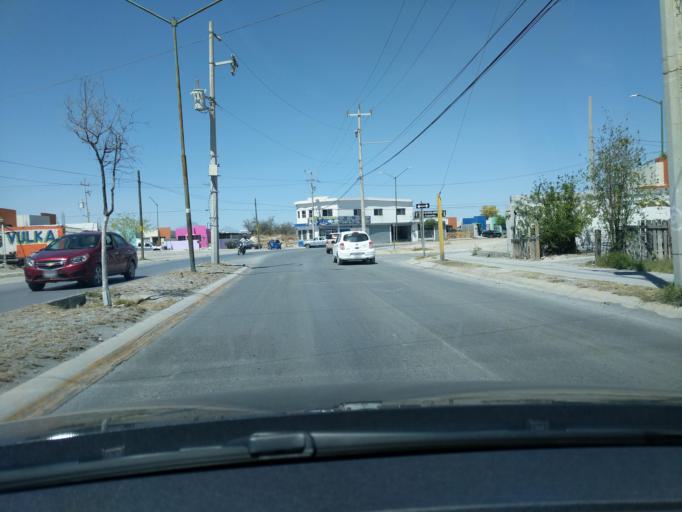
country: MX
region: Nuevo Leon
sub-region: Pesqueria
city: Colinas del Aeropuerto
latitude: 25.8139
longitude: -100.1088
